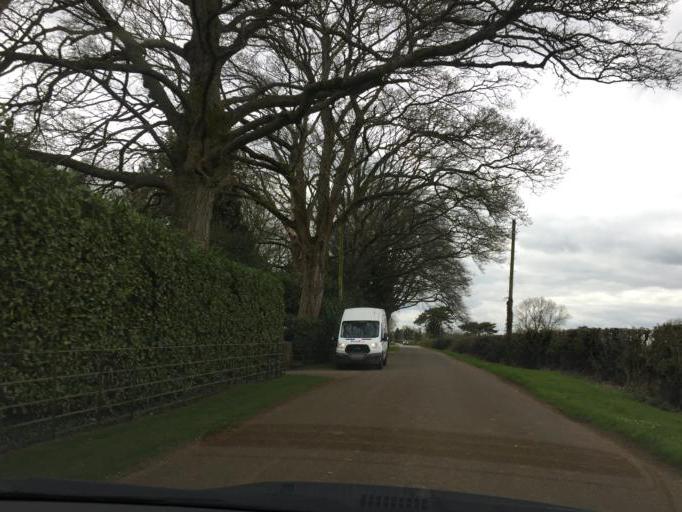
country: GB
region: England
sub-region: Oxfordshire
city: Hanwell
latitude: 52.1079
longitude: -1.4341
